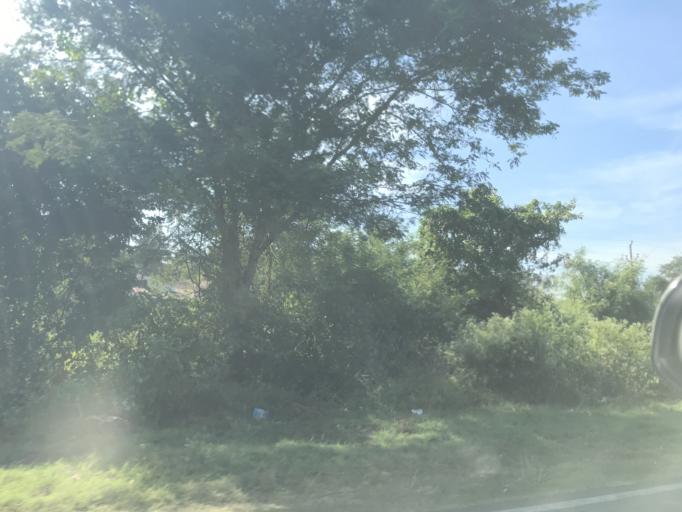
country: IN
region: Karnataka
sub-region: Mysore
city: Mysore
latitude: 12.2094
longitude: 76.5590
